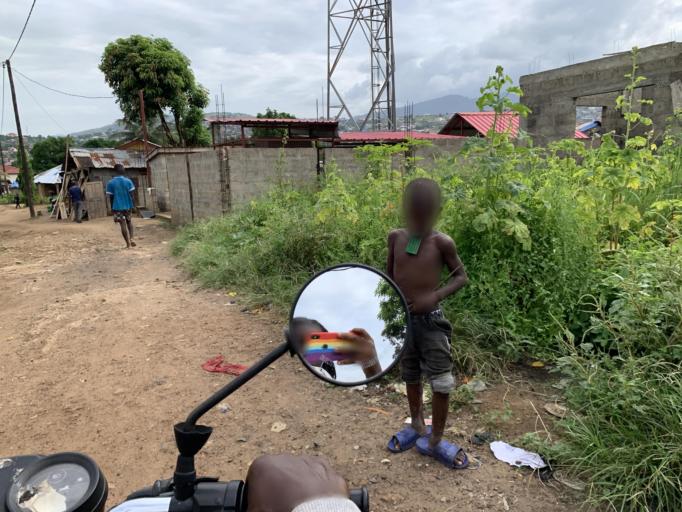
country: SL
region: Western Area
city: Hastings
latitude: 8.3966
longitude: -13.1182
